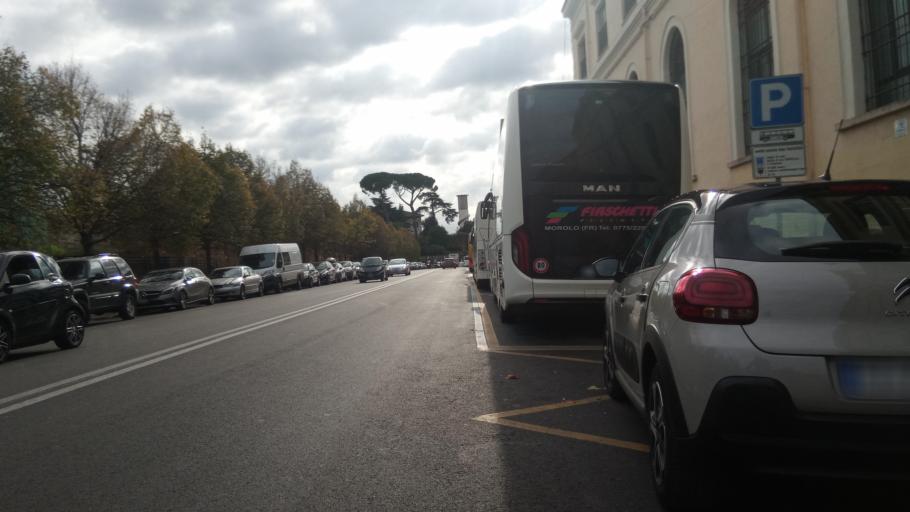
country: IT
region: Latium
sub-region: Citta metropolitana di Roma Capitale
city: Rome
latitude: 41.9004
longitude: 12.5082
